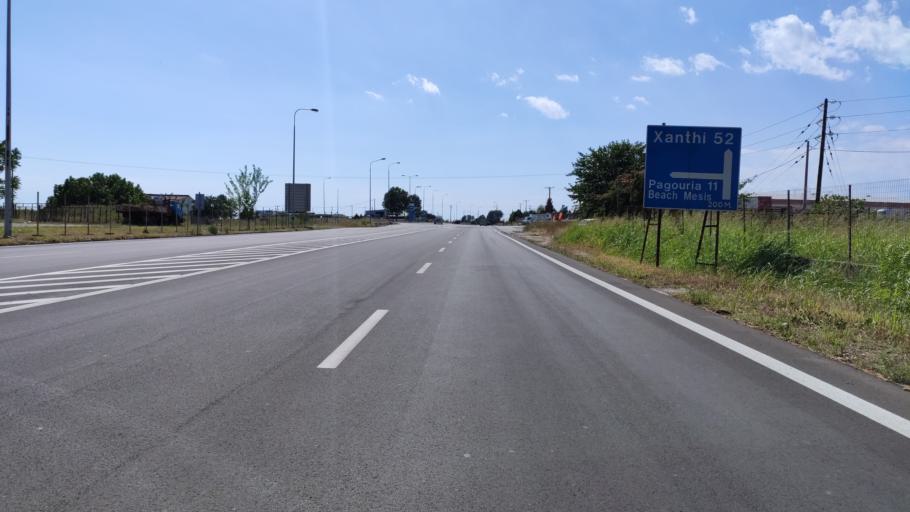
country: GR
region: East Macedonia and Thrace
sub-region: Nomos Rodopis
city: Komotini
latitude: 41.1089
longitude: 25.3609
